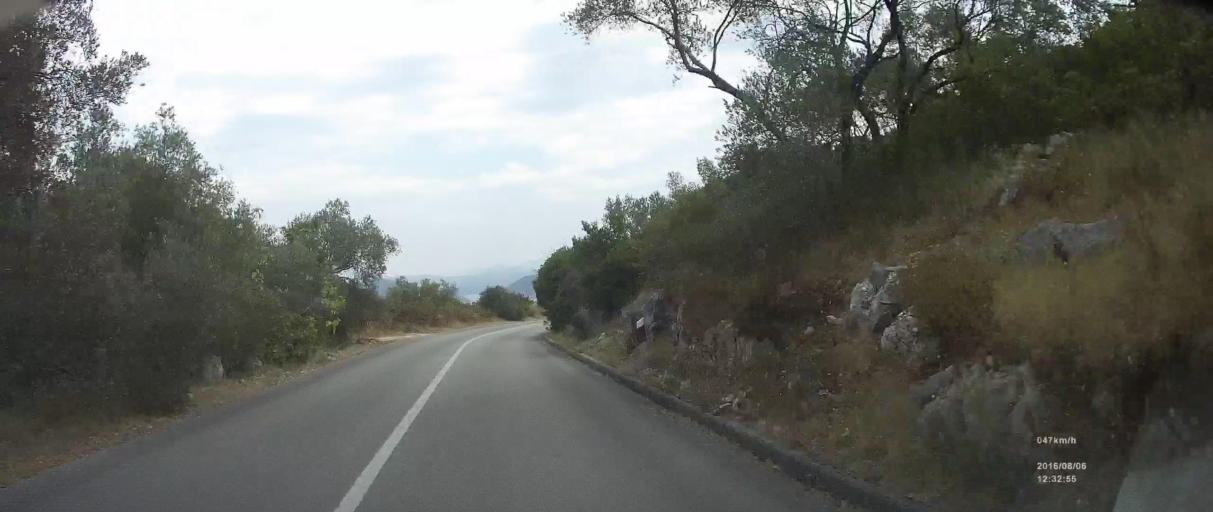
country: HR
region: Dubrovacko-Neretvanska
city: Ston
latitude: 42.7125
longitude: 17.7164
